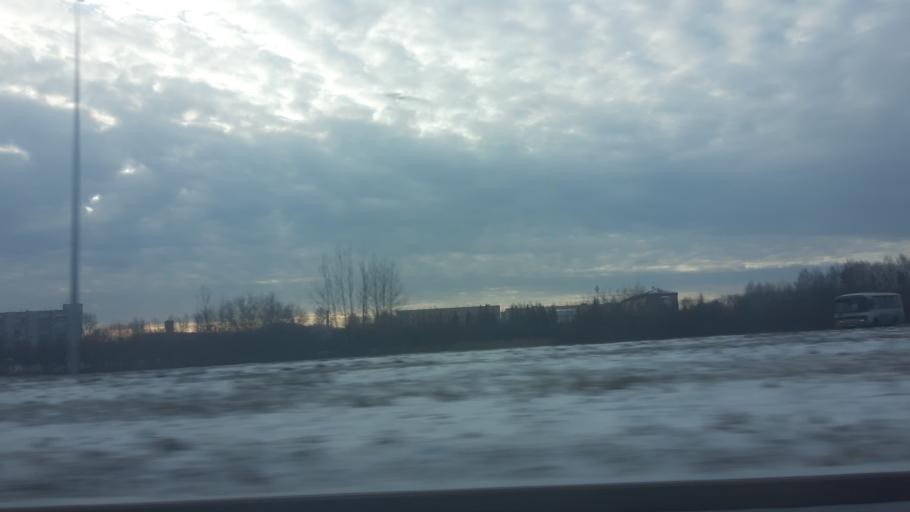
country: RU
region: Tjumen
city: Moskovskiy
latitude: 57.1859
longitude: 65.3603
